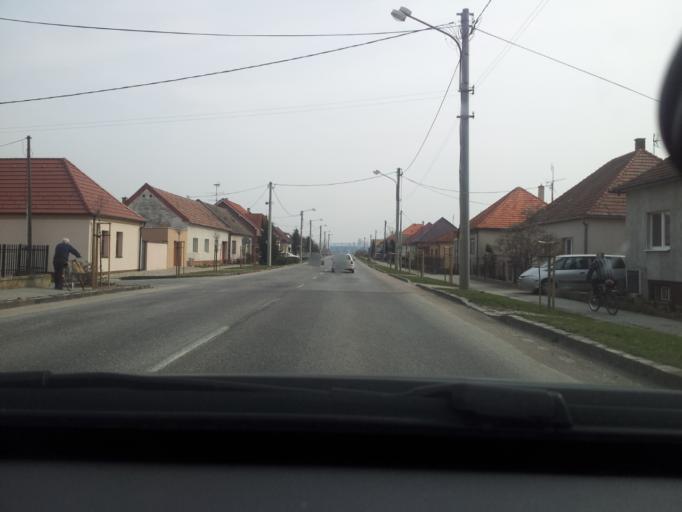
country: SK
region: Trnavsky
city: Leopoldov
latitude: 48.4398
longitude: 17.7171
